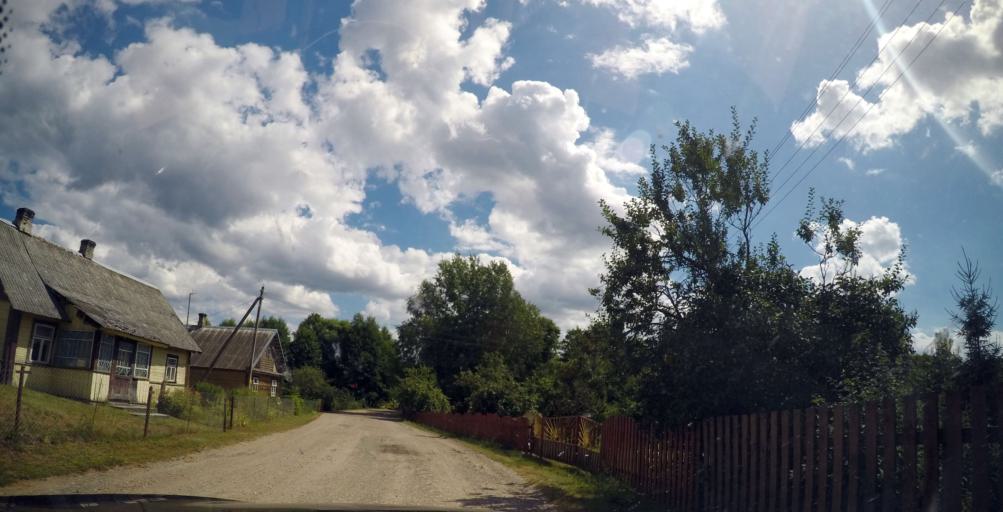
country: BY
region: Grodnenskaya
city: Skidal'
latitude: 53.8212
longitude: 24.2445
